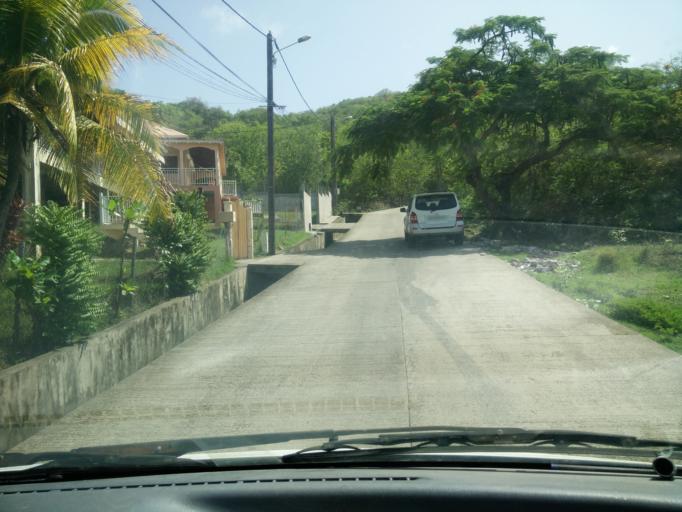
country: GP
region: Guadeloupe
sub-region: Guadeloupe
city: Terre-de-Bas
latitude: 15.8568
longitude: -61.6250
